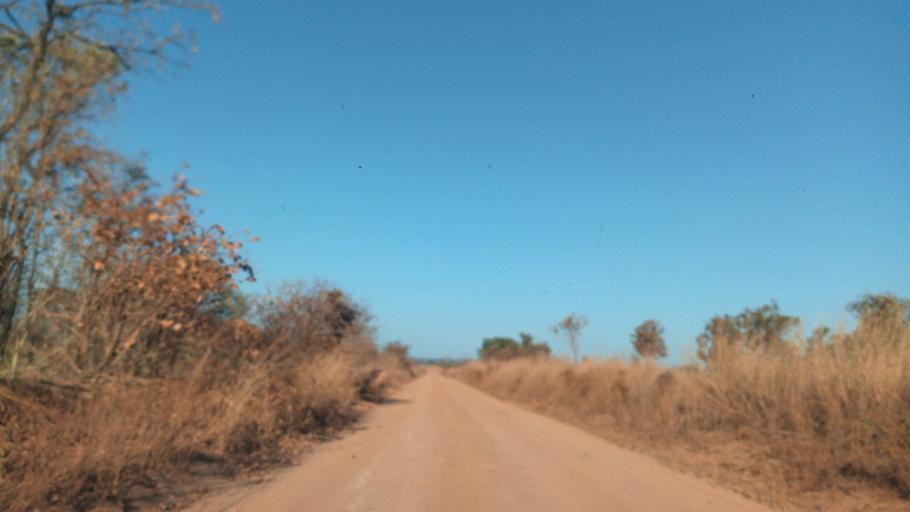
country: ZM
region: Luapula
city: Mwense
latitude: -10.5101
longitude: 28.4690
